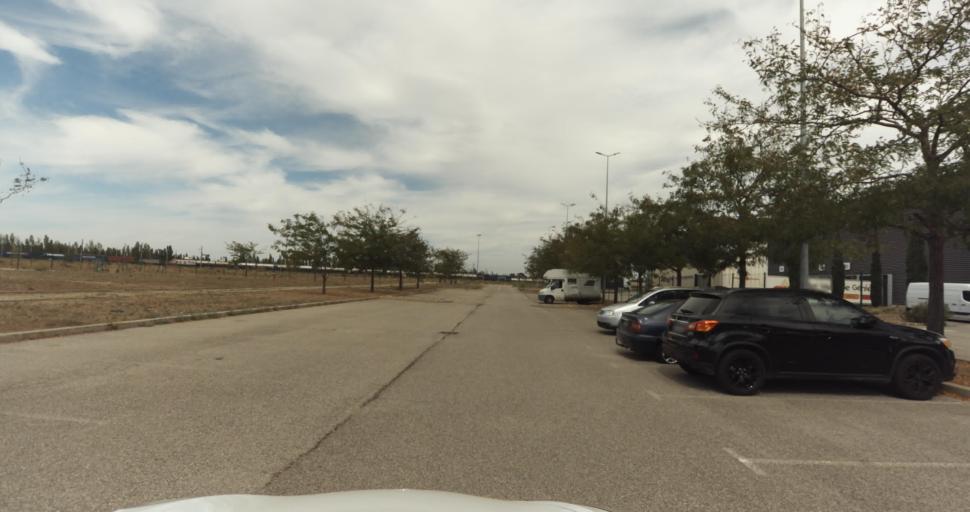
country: FR
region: Provence-Alpes-Cote d'Azur
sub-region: Departement des Bouches-du-Rhone
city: Miramas
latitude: 43.6039
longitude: 4.9921
